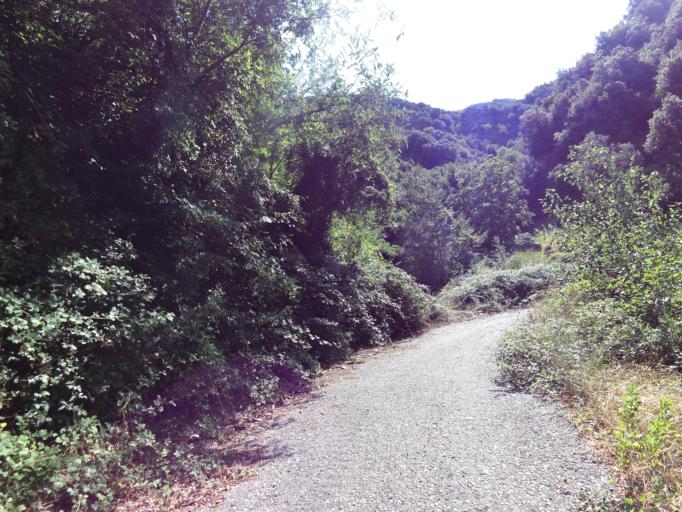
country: IT
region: Calabria
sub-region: Provincia di Reggio Calabria
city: Pazzano
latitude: 38.4710
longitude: 16.4239
